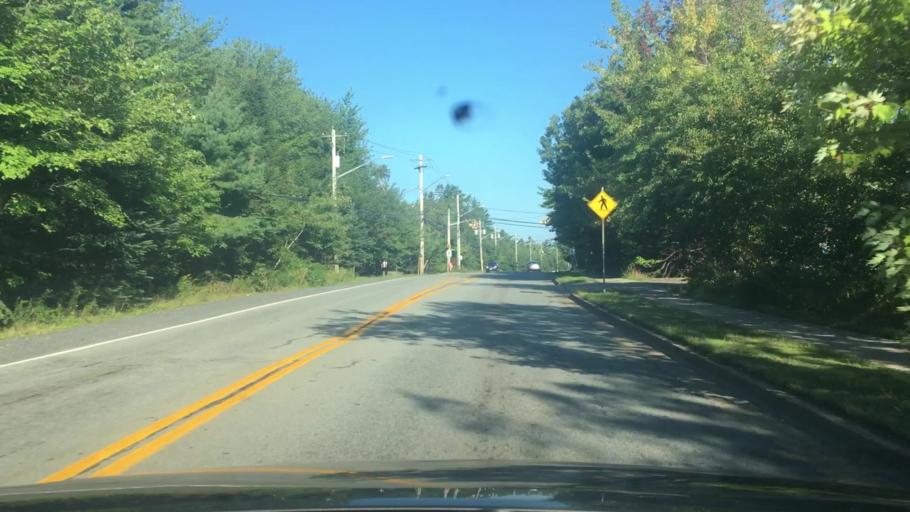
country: CA
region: Nova Scotia
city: Dartmouth
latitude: 44.7180
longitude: -63.6846
